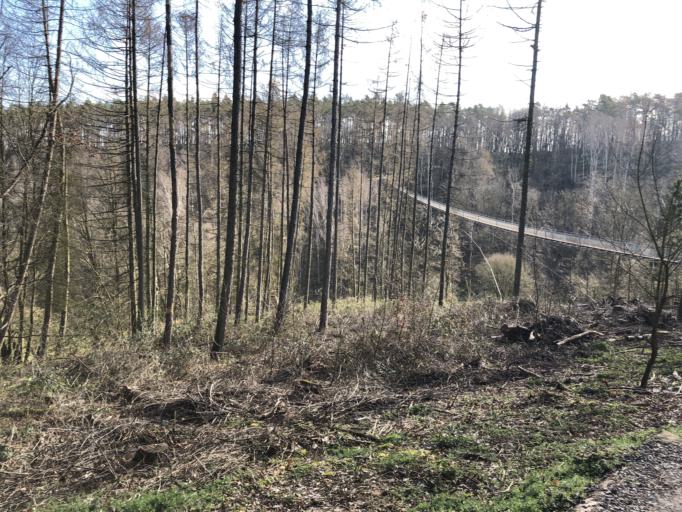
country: DE
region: Thuringia
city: Reinsdorf
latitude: 51.3127
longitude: 11.2828
